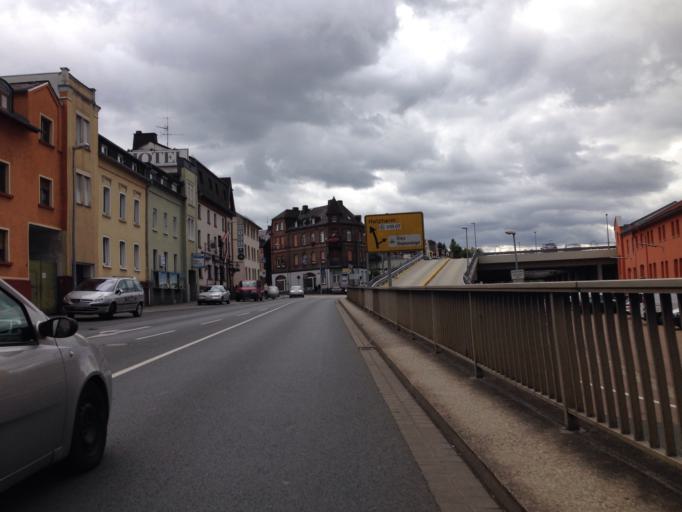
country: DE
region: Hesse
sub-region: Regierungsbezirk Giessen
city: Limburg an der Lahn
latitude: 50.3840
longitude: 8.0633
